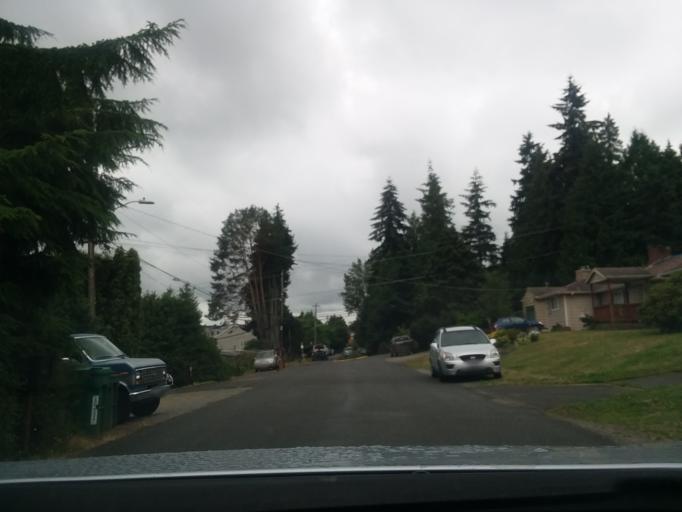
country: US
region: Washington
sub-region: King County
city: Lake Forest Park
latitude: 47.7127
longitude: -122.3018
